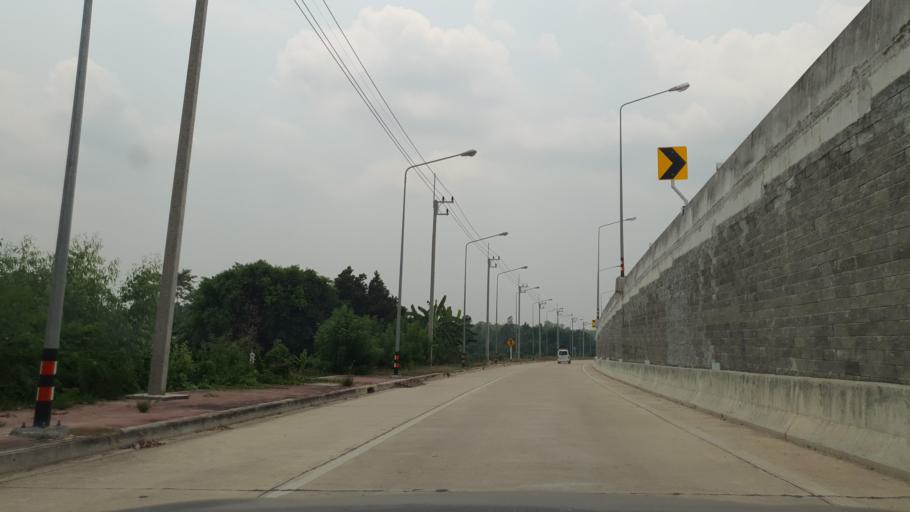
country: TH
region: Chon Buri
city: Phatthaya
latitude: 12.8393
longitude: 100.9610
